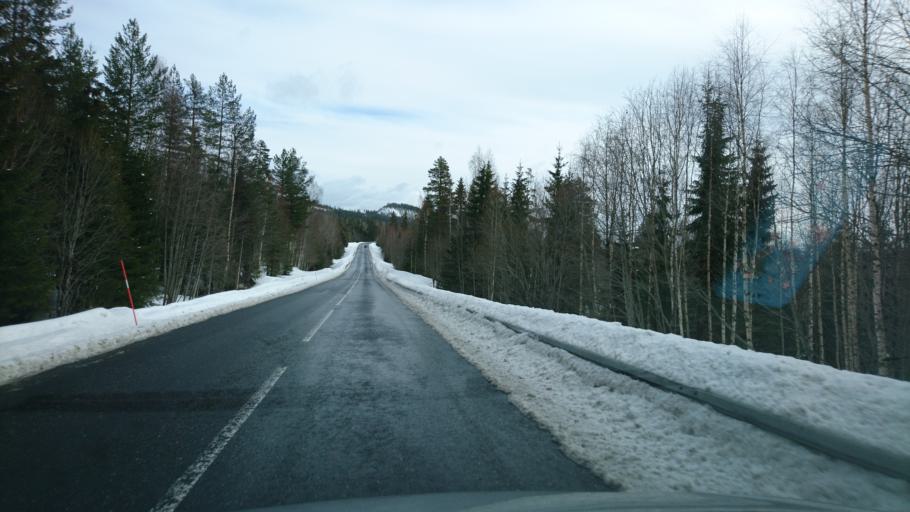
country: SE
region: Vaesternorrland
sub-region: Solleftea Kommun
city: As
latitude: 63.2948
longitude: 16.6872
